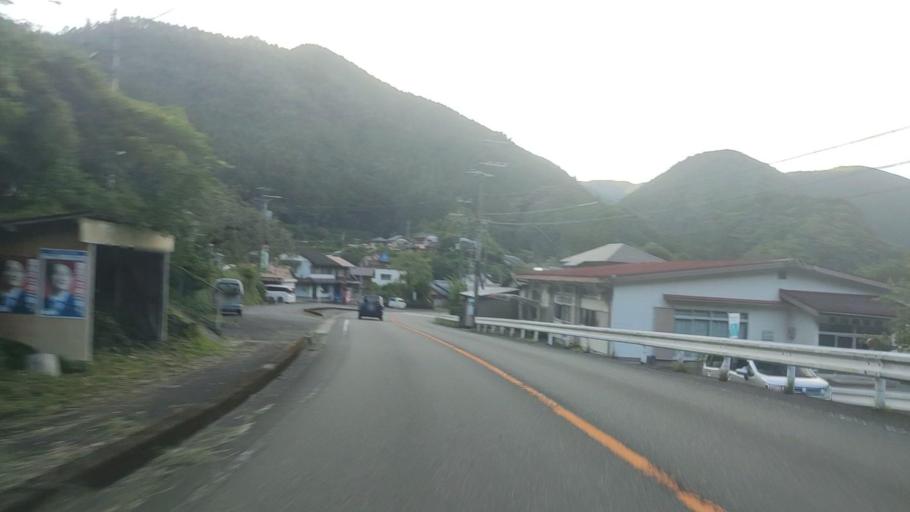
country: JP
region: Wakayama
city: Tanabe
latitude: 33.8119
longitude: 135.5498
